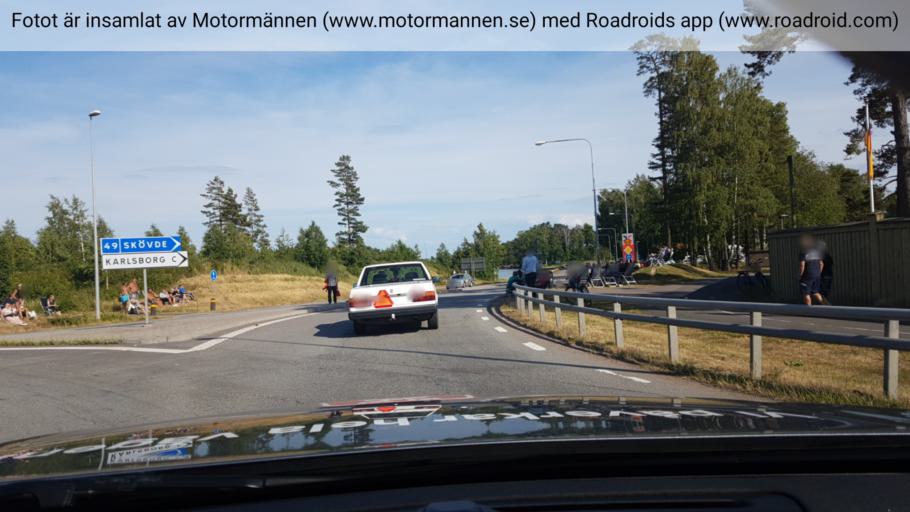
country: SE
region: Vaestra Goetaland
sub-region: Karlsborgs Kommun
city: Karlsborg
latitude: 58.5455
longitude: 14.5008
